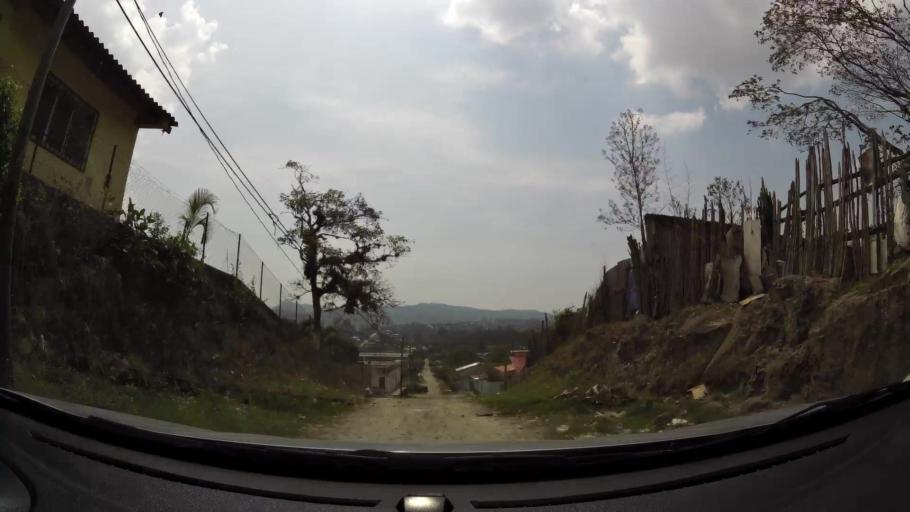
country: HN
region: Comayagua
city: Siguatepeque
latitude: 14.5997
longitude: -87.8289
